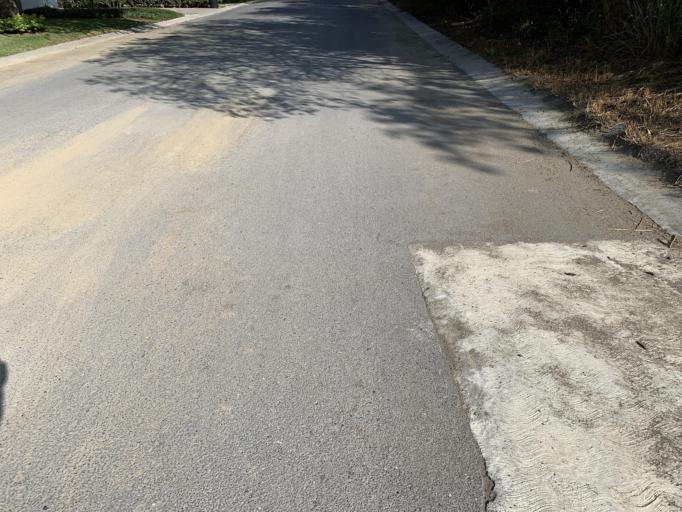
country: MX
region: Nuevo Leon
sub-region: Juarez
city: Bosques de San Pedro
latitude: 25.5132
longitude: -100.1895
